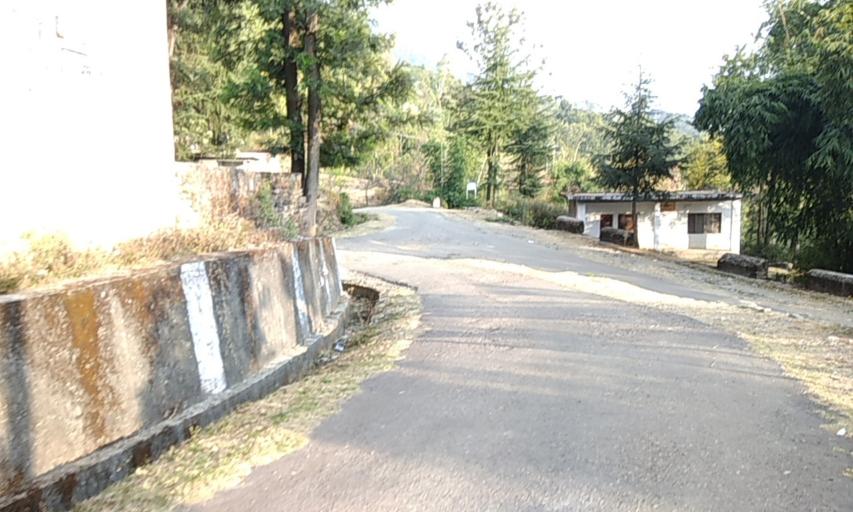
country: IN
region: Himachal Pradesh
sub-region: Kangra
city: Palampur
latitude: 32.1192
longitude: 76.5852
